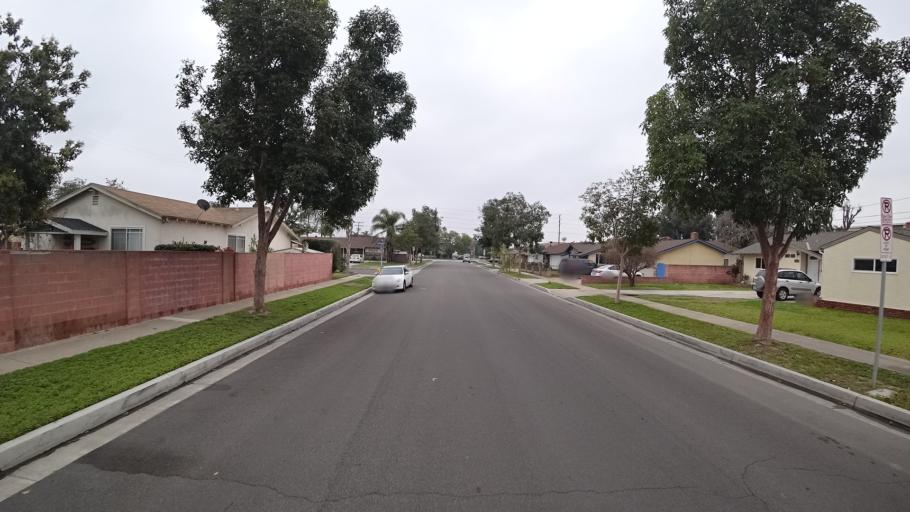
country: US
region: California
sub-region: Orange County
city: Stanton
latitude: 33.8185
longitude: -118.0076
